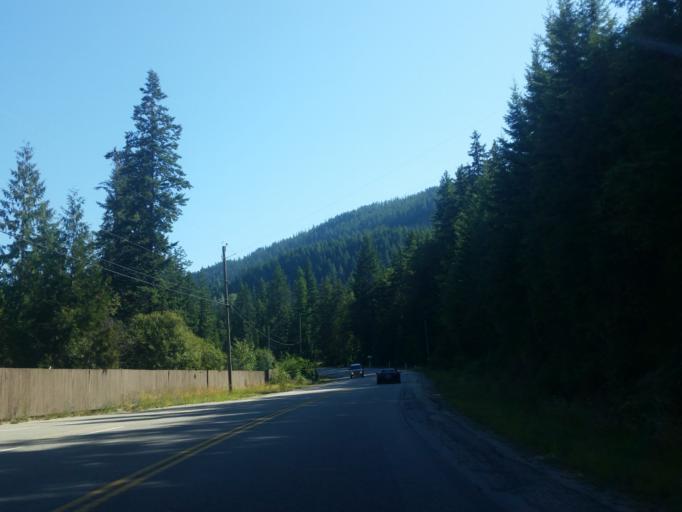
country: CA
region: British Columbia
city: Sicamous
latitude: 50.7631
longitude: -119.0118
